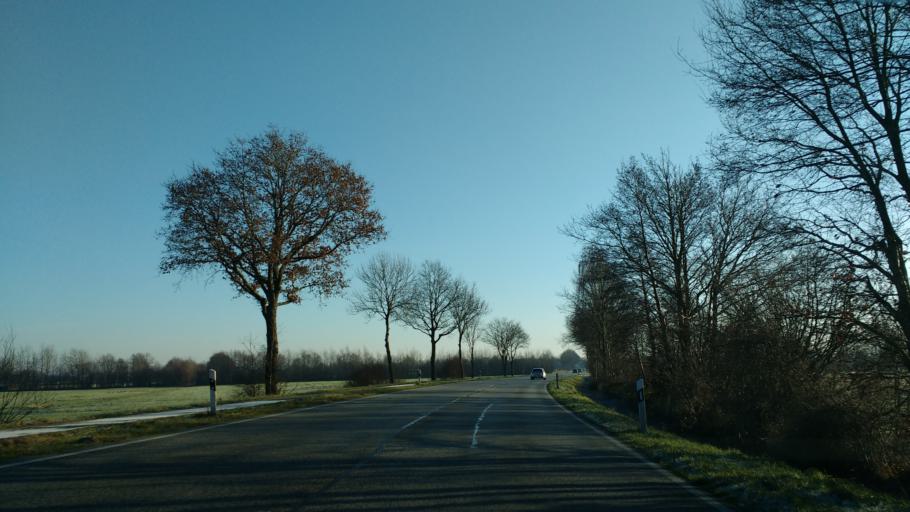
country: DE
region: Schleswig-Holstein
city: Wasbek
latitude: 54.0719
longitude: 9.8714
